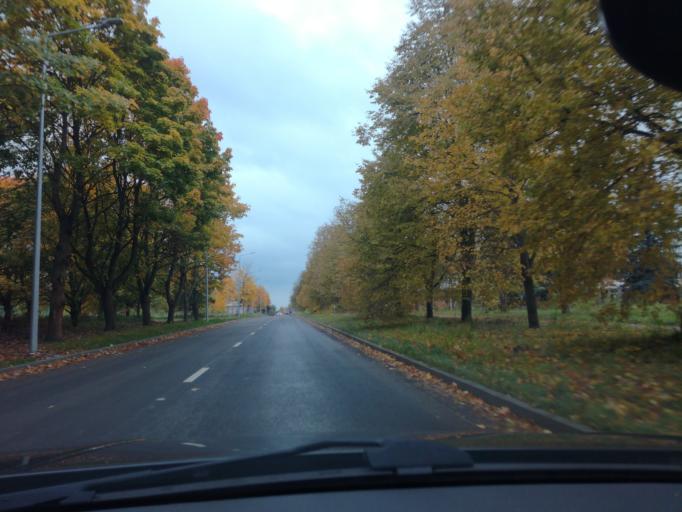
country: LT
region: Alytaus apskritis
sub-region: Alytus
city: Alytus
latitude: 54.4190
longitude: 24.0185
